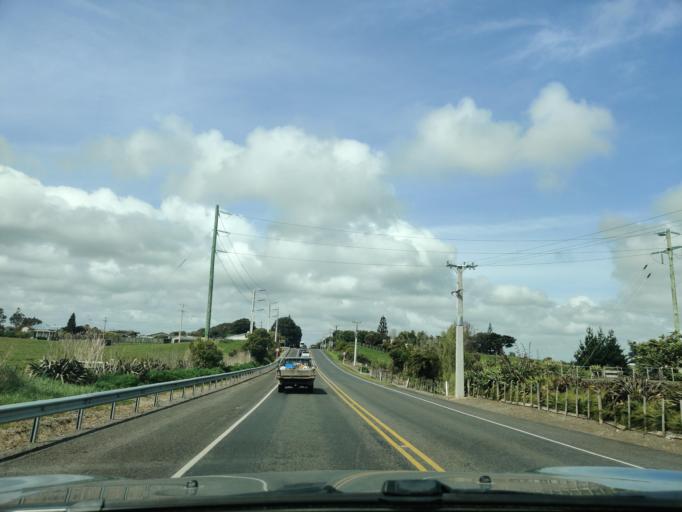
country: NZ
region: Taranaki
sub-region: South Taranaki District
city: Patea
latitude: -39.7651
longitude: 174.6217
